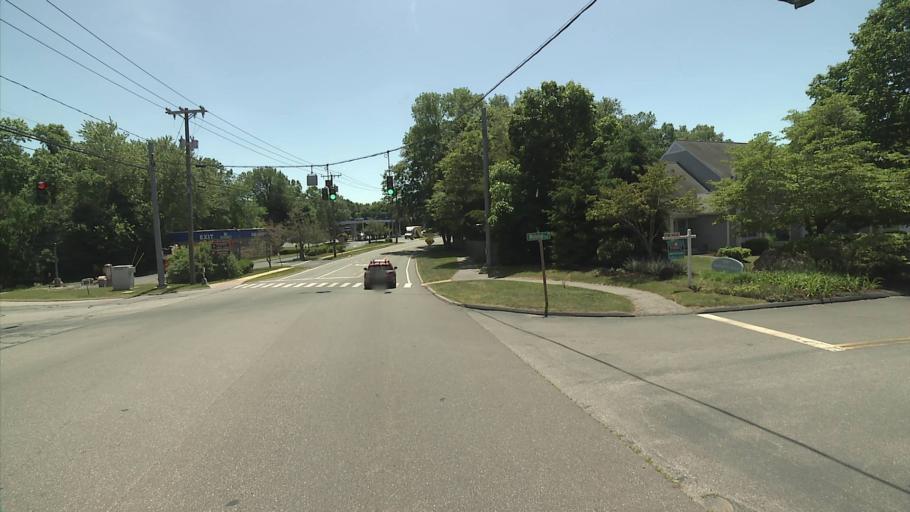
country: US
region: Connecticut
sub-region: New London County
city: Old Mystic
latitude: 41.3804
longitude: -71.9563
